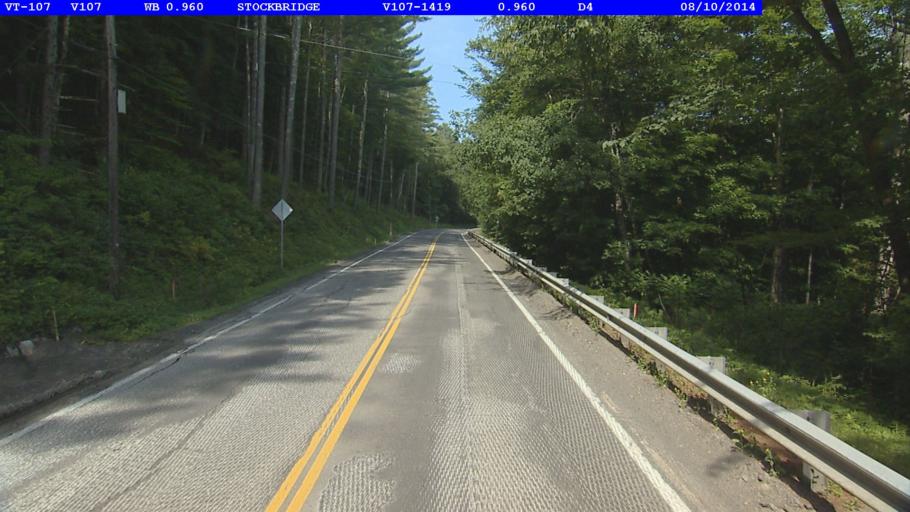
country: US
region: Vermont
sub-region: Orange County
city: Randolph
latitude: 43.7674
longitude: -72.7474
